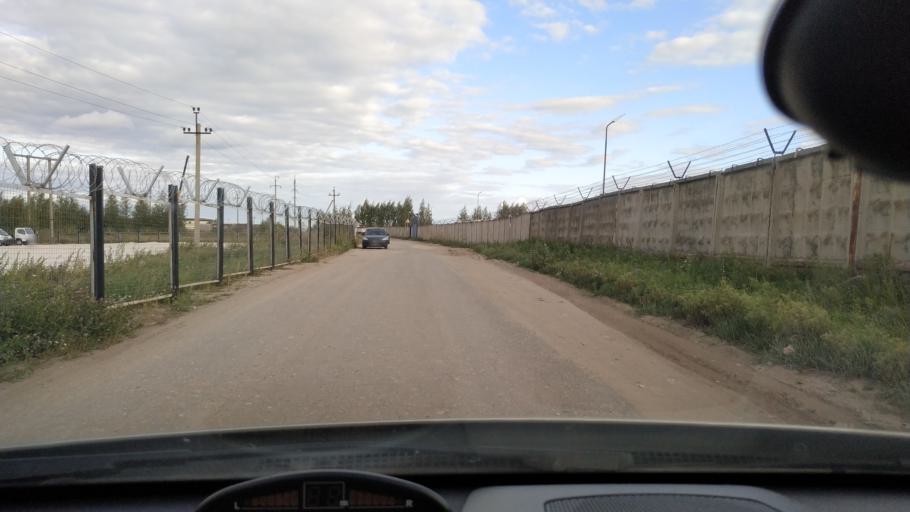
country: RU
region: Rjazan
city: Polyany
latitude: 54.5775
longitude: 39.8420
